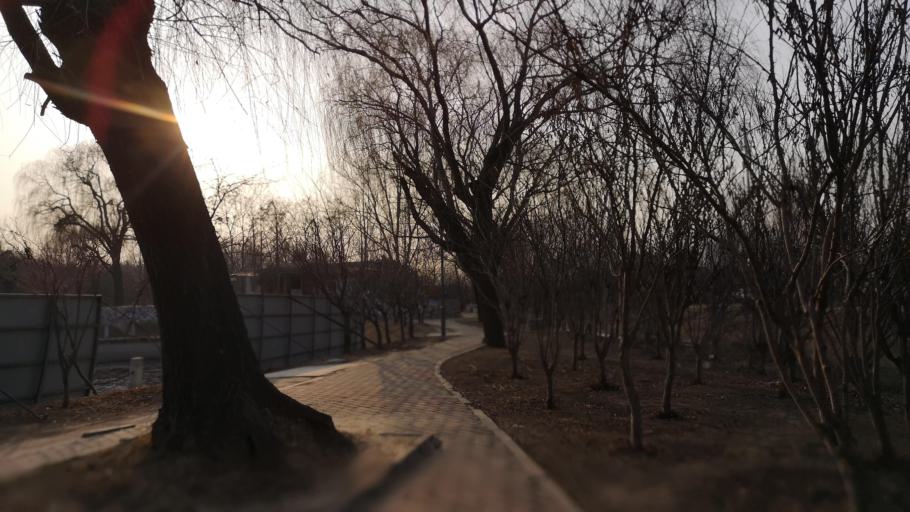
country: CN
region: Henan Sheng
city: Zhongyuanlu
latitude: 35.7455
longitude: 115.0646
